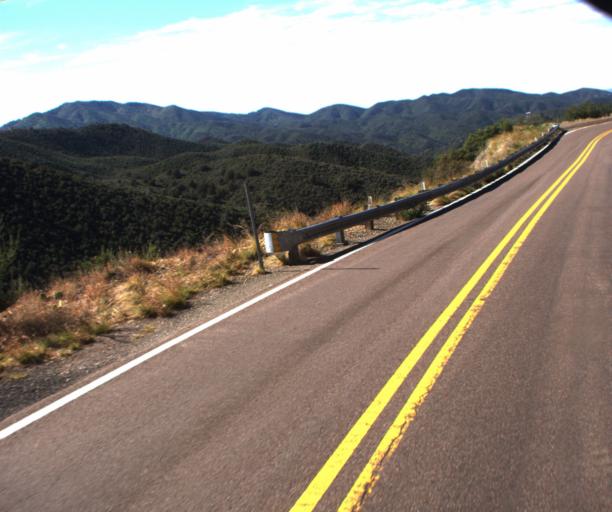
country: US
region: Arizona
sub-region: Yavapai County
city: Prescott
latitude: 34.4664
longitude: -112.5147
